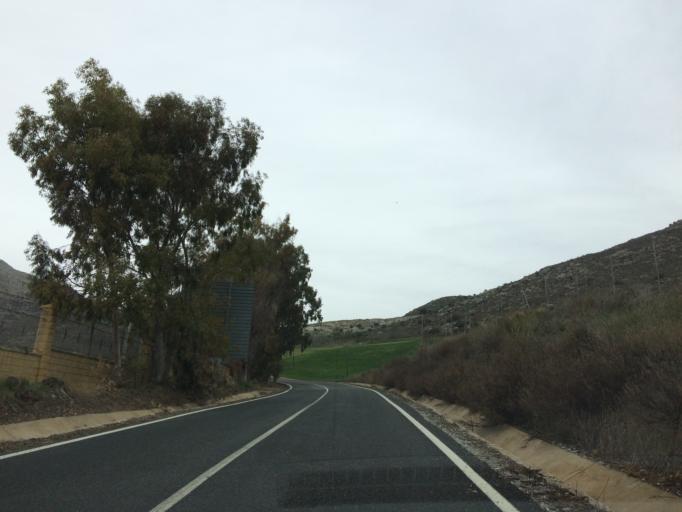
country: ES
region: Andalusia
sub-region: Provincia de Malaga
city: Casabermeja
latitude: 36.9558
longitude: -4.4424
